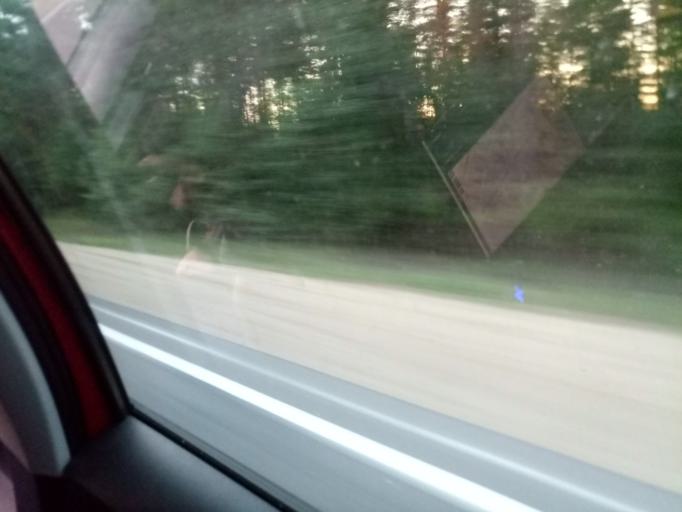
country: RU
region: Moskovskaya
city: Noginsk-9
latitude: 56.0758
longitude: 38.5701
